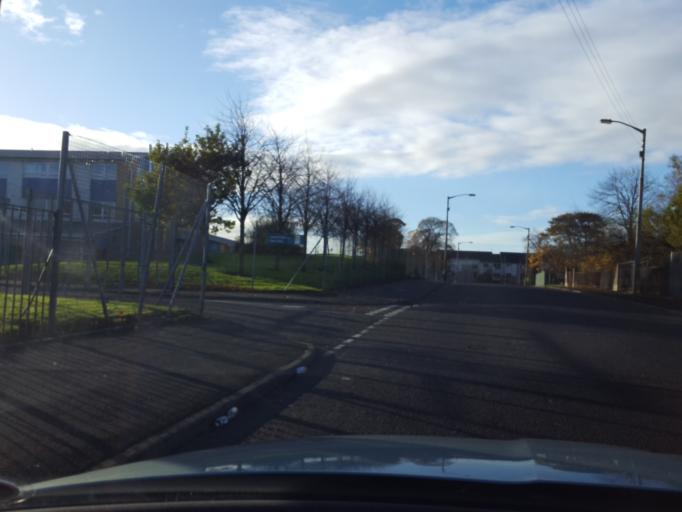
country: GB
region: Scotland
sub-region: North Lanarkshire
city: Chryston
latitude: 55.8695
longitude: -4.1085
